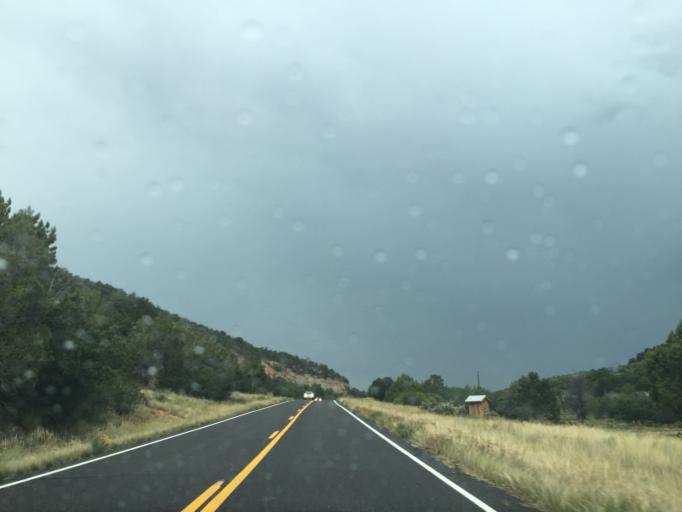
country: US
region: Utah
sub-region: Washington County
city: Hildale
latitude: 37.2375
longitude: -112.8526
